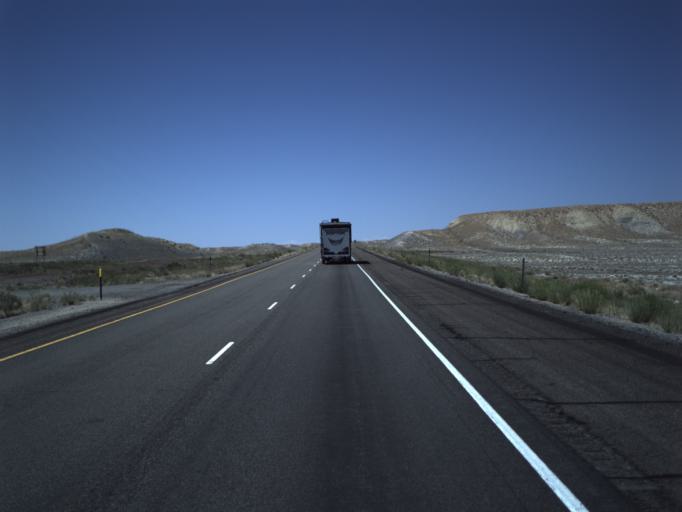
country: US
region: Utah
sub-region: Grand County
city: Moab
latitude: 38.9428
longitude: -109.6255
